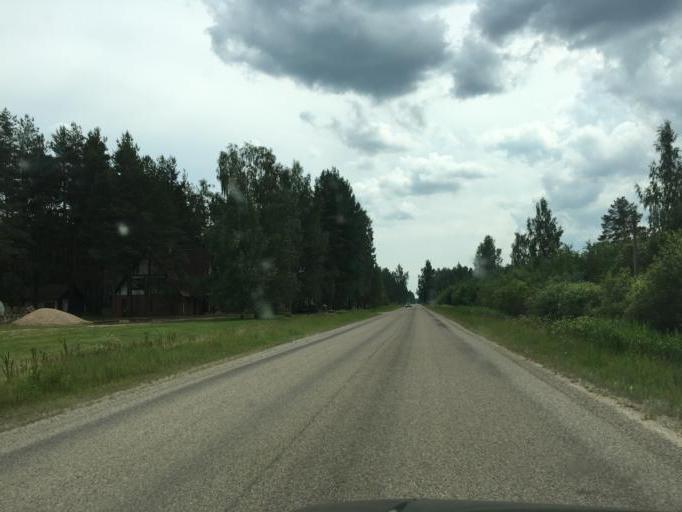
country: LV
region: Rugaju
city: Rugaji
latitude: 56.8312
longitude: 27.0938
